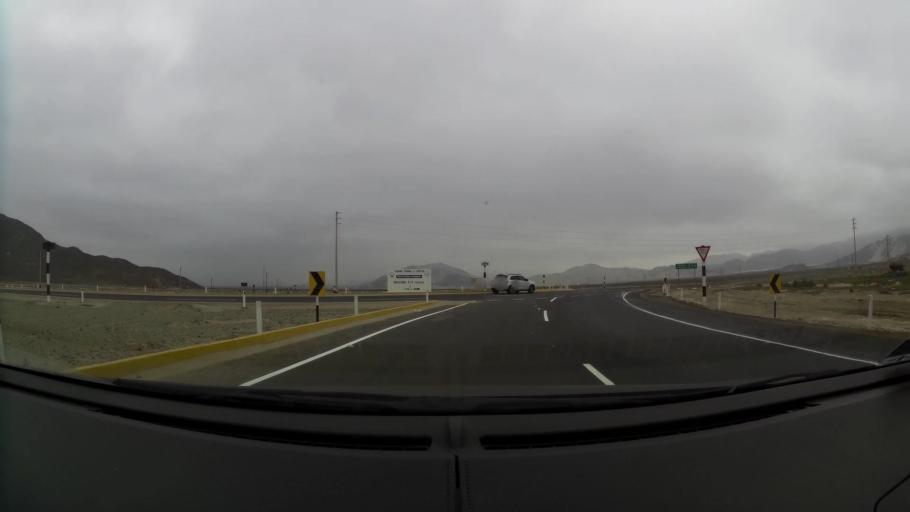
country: PE
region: La Libertad
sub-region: Viru
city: Chao
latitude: -8.6489
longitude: -78.6204
